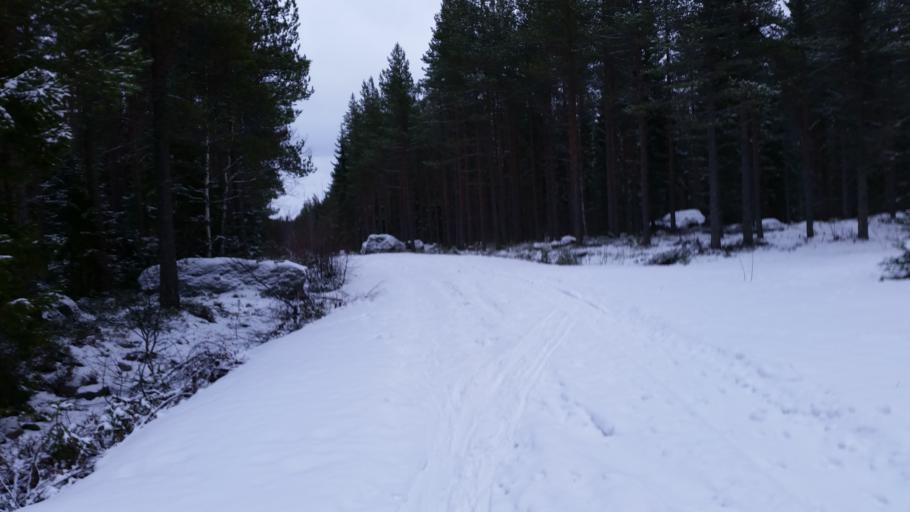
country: SE
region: Vaesterbotten
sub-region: Umea Kommun
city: Saevar
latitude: 63.9177
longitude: 20.7728
